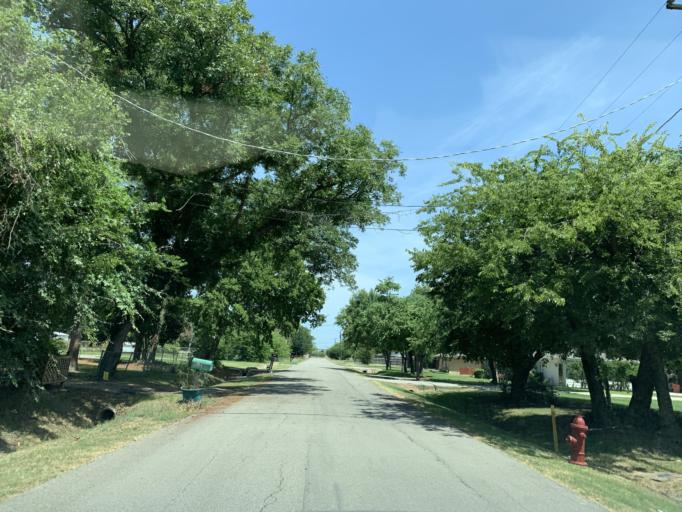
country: US
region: Texas
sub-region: Dallas County
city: Cedar Hill
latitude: 32.6474
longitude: -97.0175
